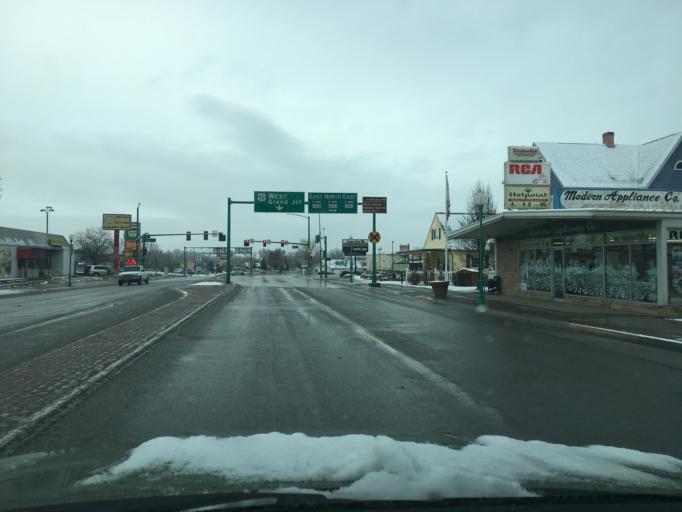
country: US
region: Colorado
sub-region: Delta County
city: Delta
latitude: 38.7444
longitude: -108.0708
